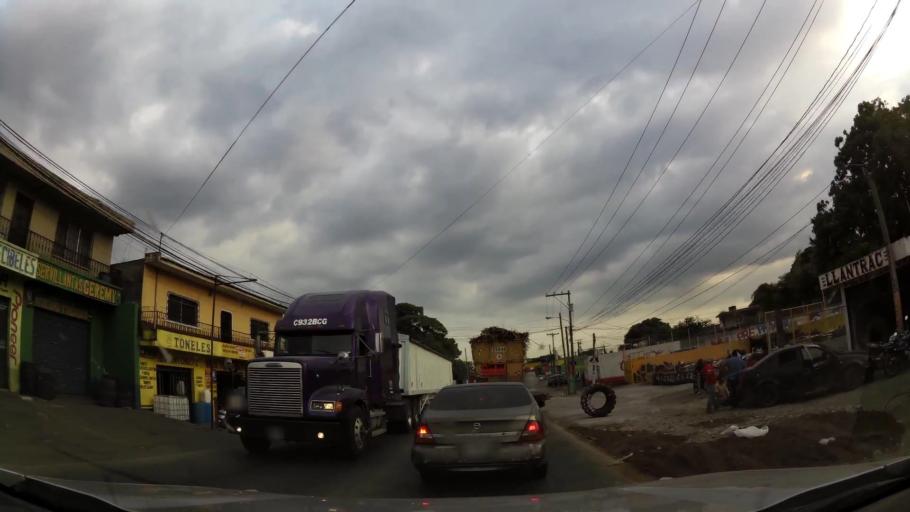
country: GT
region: Escuintla
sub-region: Municipio de Escuintla
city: Escuintla
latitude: 14.3033
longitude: -90.7812
